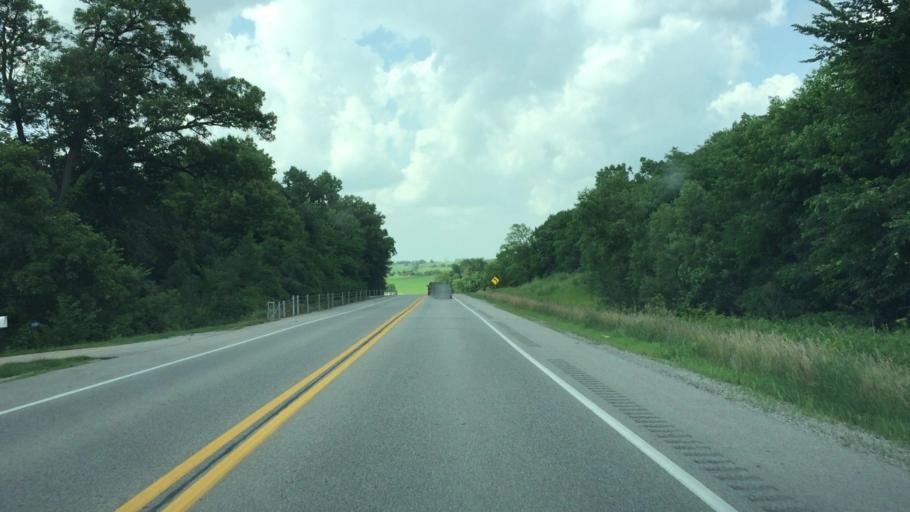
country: US
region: Iowa
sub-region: Johnson County
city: Solon
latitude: 41.7453
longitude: -91.4739
